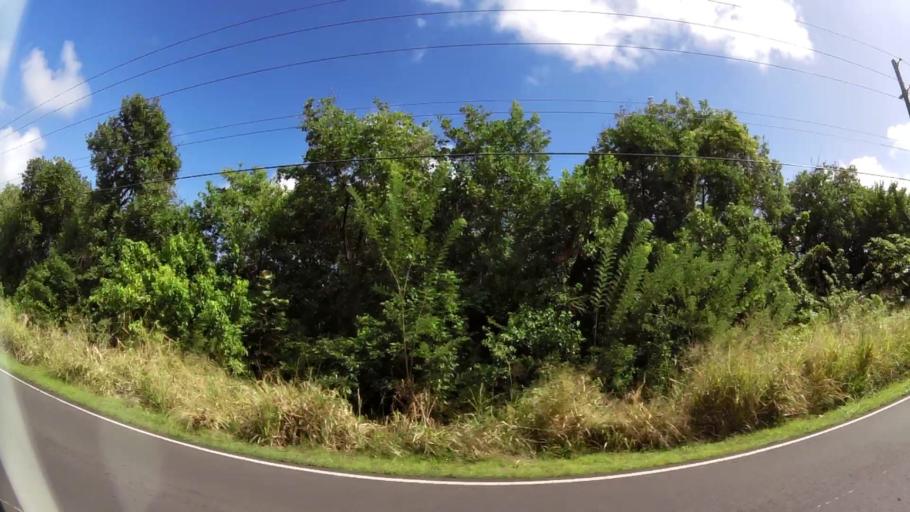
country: LC
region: Micoud Quarter
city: Micoud
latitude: 13.8051
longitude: -60.9035
